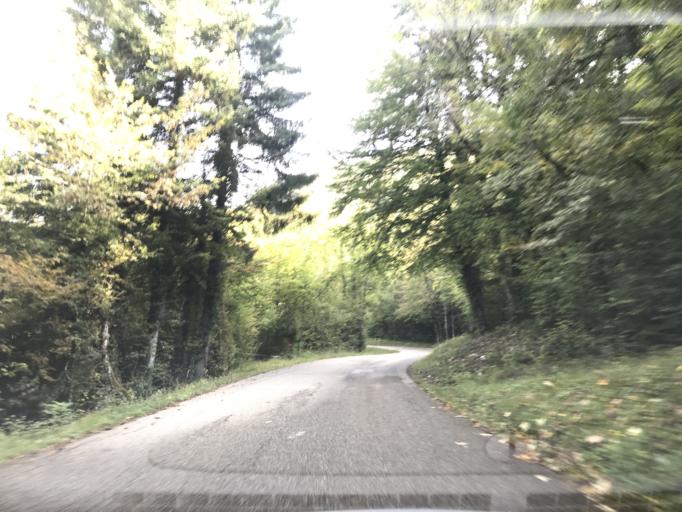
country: FR
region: Rhone-Alpes
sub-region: Departement de la Savoie
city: Novalaise
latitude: 45.6441
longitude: 5.7955
